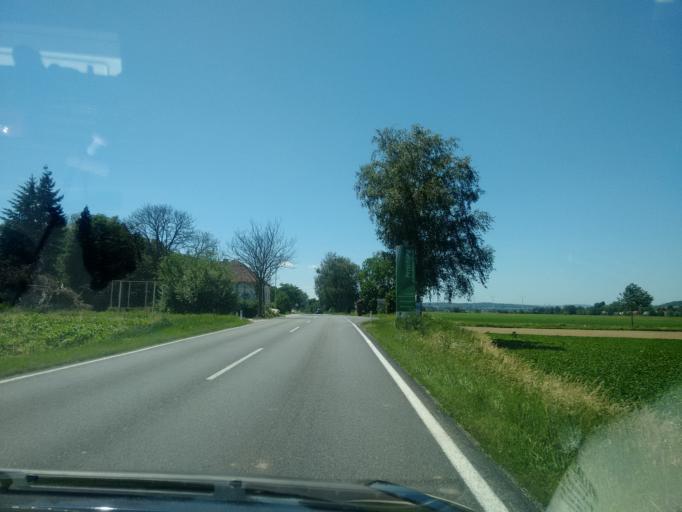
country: AT
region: Lower Austria
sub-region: Politischer Bezirk Tulln
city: Wurmla
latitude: 48.2682
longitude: 15.8280
